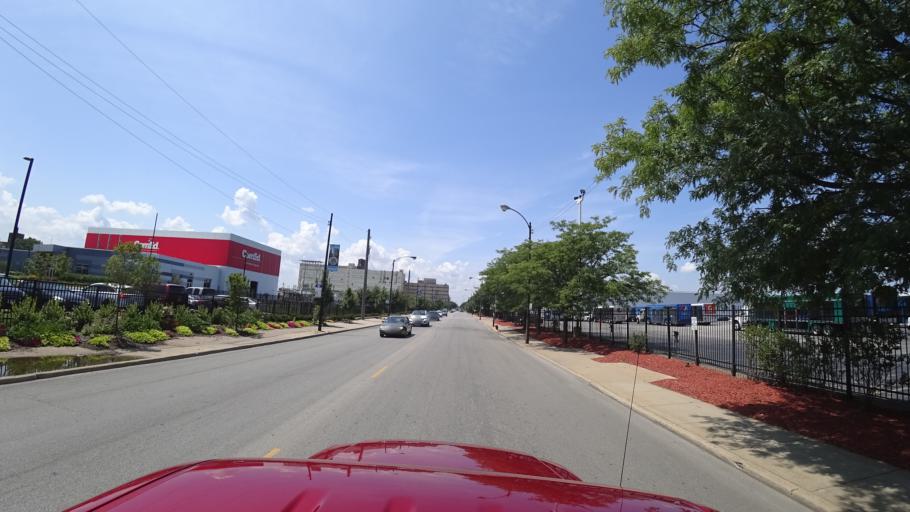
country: US
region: Illinois
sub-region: Cook County
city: Chicago
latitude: 41.8306
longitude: -87.6600
